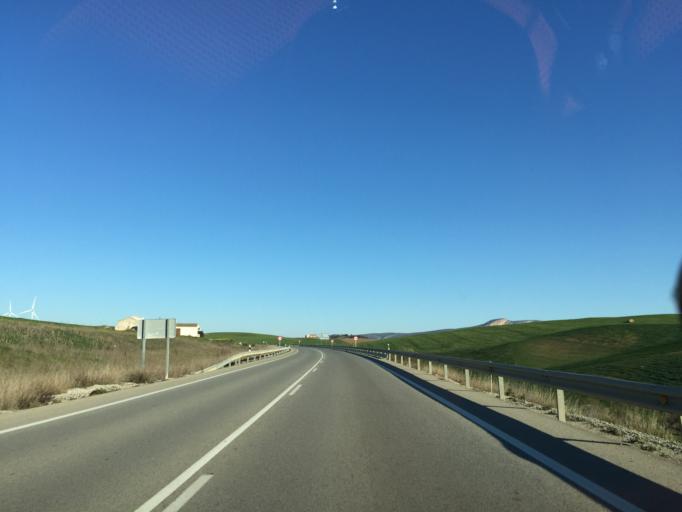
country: ES
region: Andalusia
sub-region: Provincia de Malaga
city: Ardales
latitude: 36.9187
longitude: -4.8426
